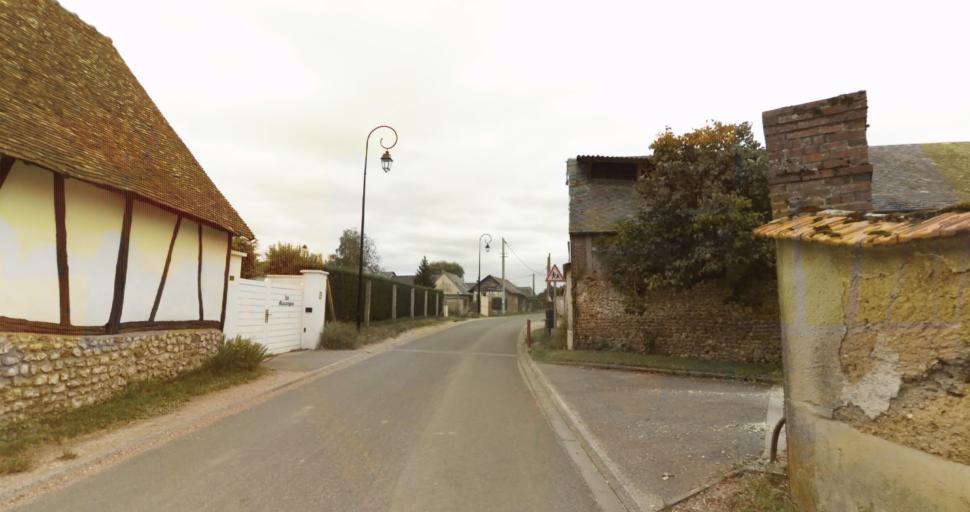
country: FR
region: Haute-Normandie
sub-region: Departement de l'Eure
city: Marcilly-sur-Eure
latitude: 48.9311
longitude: 1.2693
